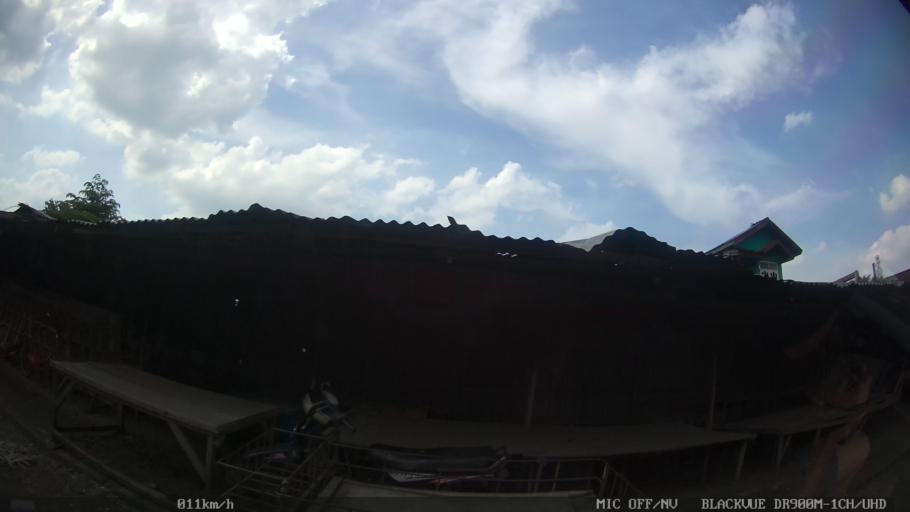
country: ID
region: North Sumatra
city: Binjai
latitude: 3.6132
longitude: 98.5186
